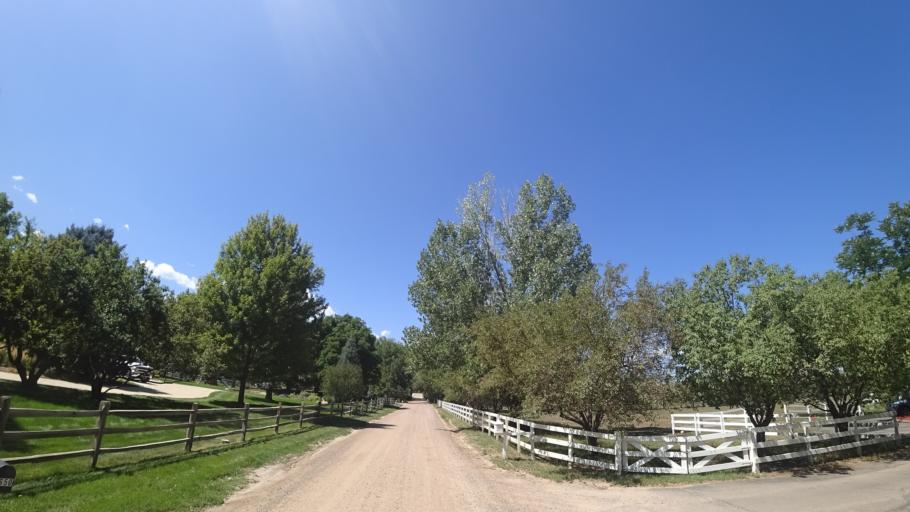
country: US
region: Colorado
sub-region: Arapahoe County
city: Greenwood Village
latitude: 39.6152
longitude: -104.9566
